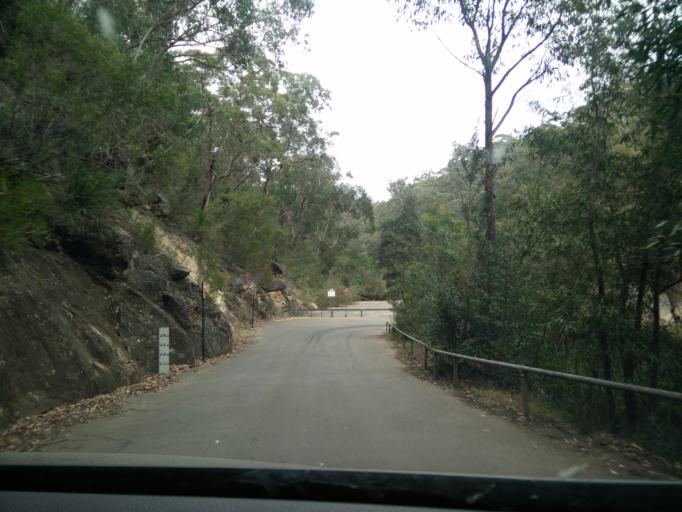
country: AU
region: New South Wales
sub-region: Blue Mountains Municipality
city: Glenbrook
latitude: -33.7787
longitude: 150.6185
